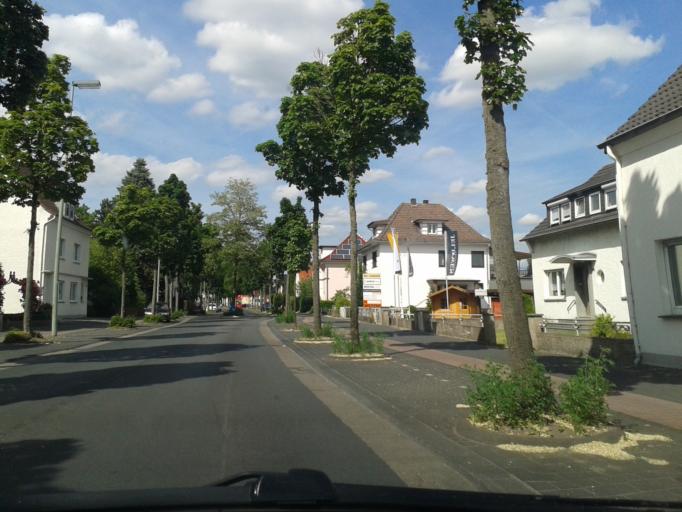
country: DE
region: North Rhine-Westphalia
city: Bad Lippspringe
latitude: 51.7869
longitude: 8.8242
